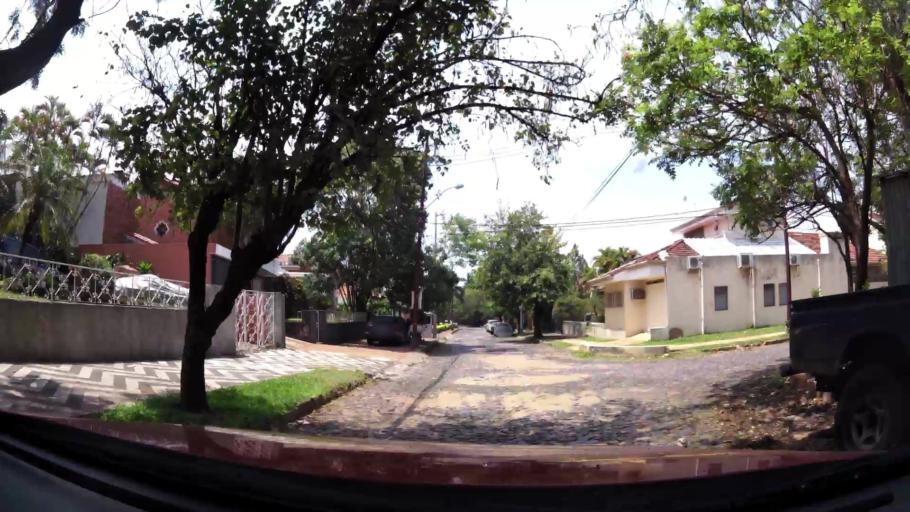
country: PY
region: Asuncion
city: Asuncion
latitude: -25.2944
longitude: -57.5958
